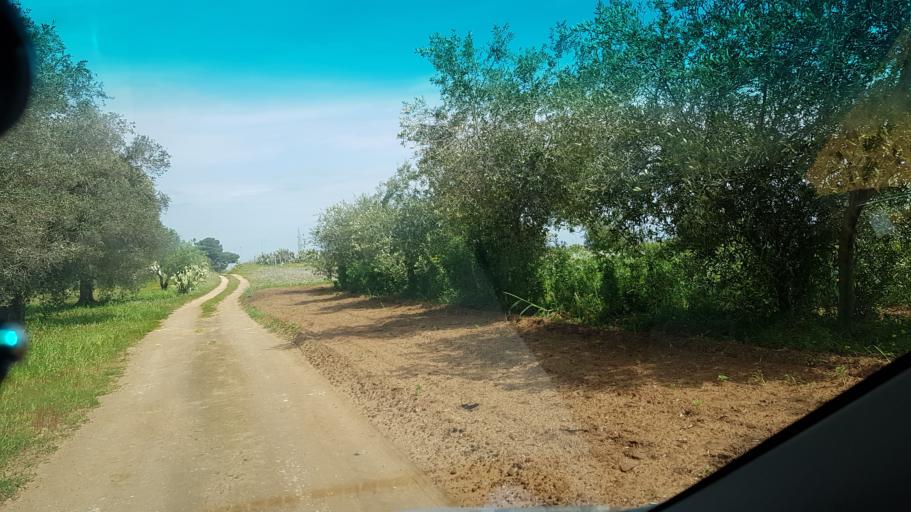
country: IT
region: Apulia
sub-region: Provincia di Brindisi
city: Mesagne
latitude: 40.6103
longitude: 17.8528
